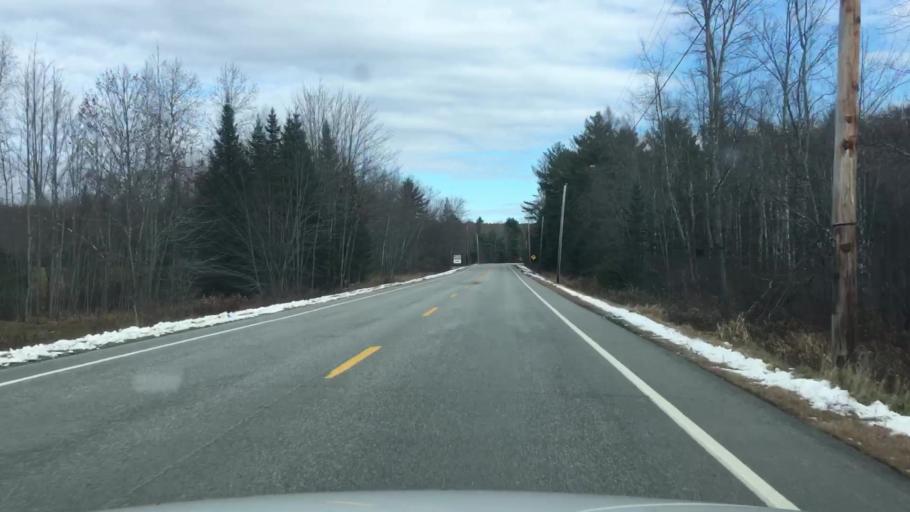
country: US
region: Maine
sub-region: Androscoggin County
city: Leeds
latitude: 44.3474
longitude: -70.1195
